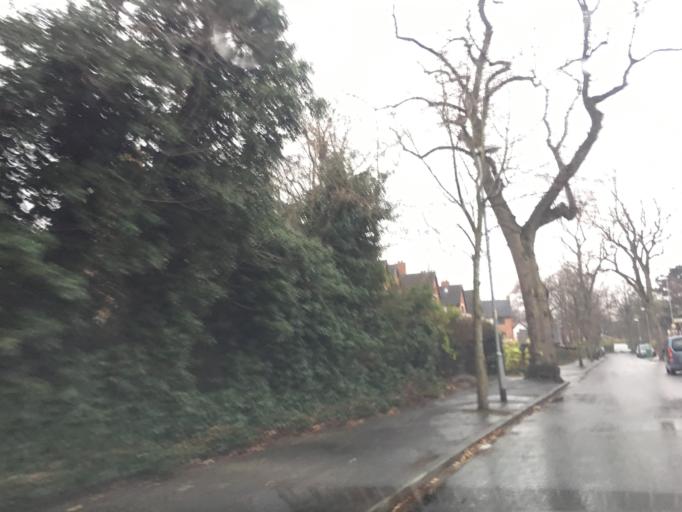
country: GB
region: England
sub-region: Manchester
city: Chorlton cum Hardy
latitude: 53.4254
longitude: -2.2595
